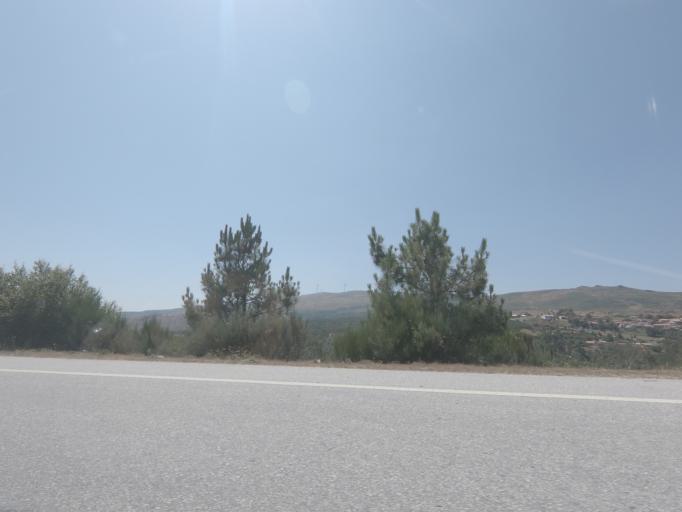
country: PT
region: Viseu
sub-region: Castro Daire
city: Castro Daire
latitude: 40.9775
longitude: -7.8872
